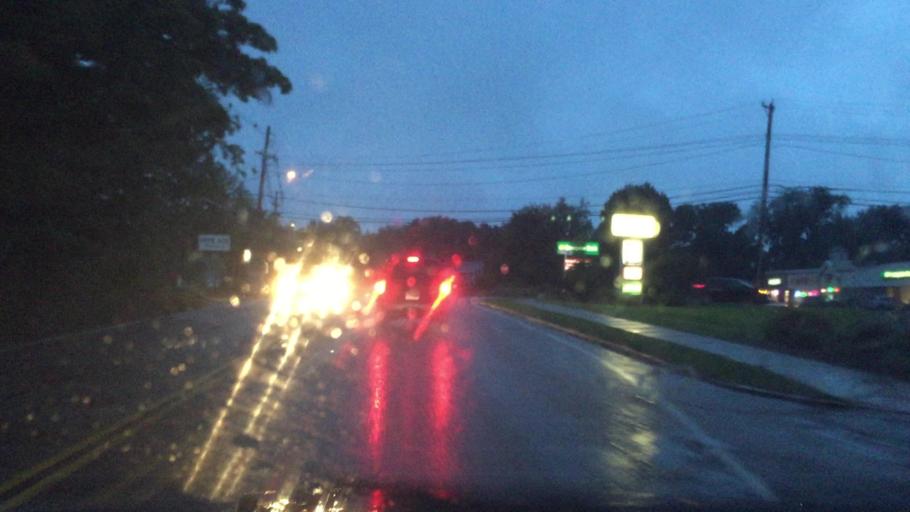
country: US
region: Massachusetts
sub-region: Middlesex County
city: Dracut
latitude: 42.6461
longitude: -71.2703
